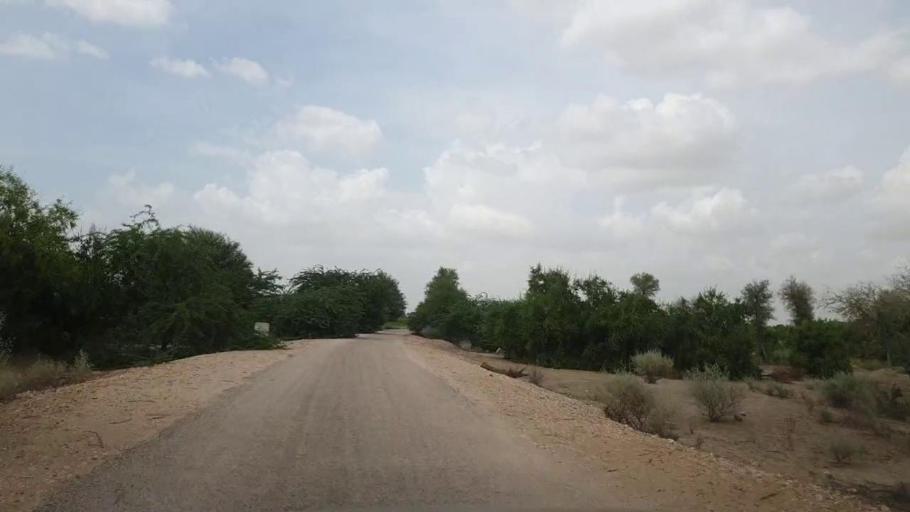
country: PK
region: Sindh
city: Kot Diji
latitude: 27.2206
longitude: 69.0841
